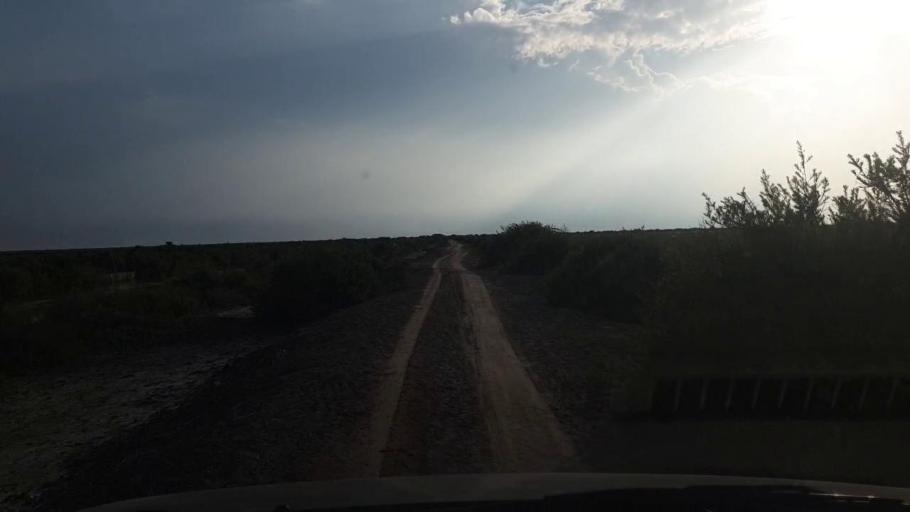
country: PK
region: Sindh
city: Badin
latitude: 24.4324
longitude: 68.6700
